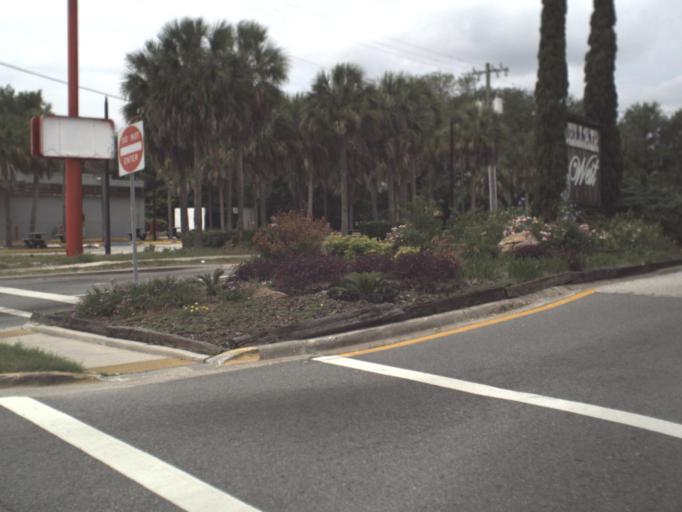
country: US
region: Florida
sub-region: Clay County
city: Bellair-Meadowbrook Terrace
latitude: 30.1722
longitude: -81.7466
